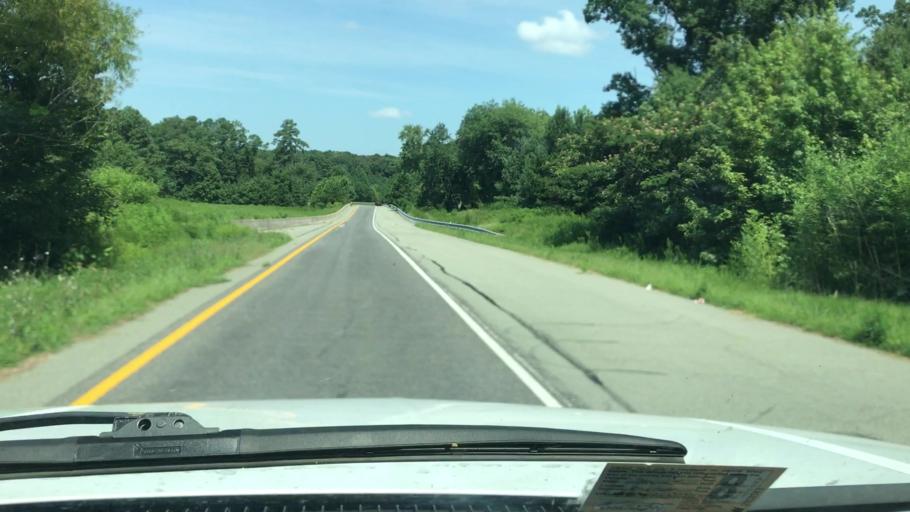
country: US
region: Virginia
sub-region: Henrico County
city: Short Pump
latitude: 37.6012
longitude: -77.6630
